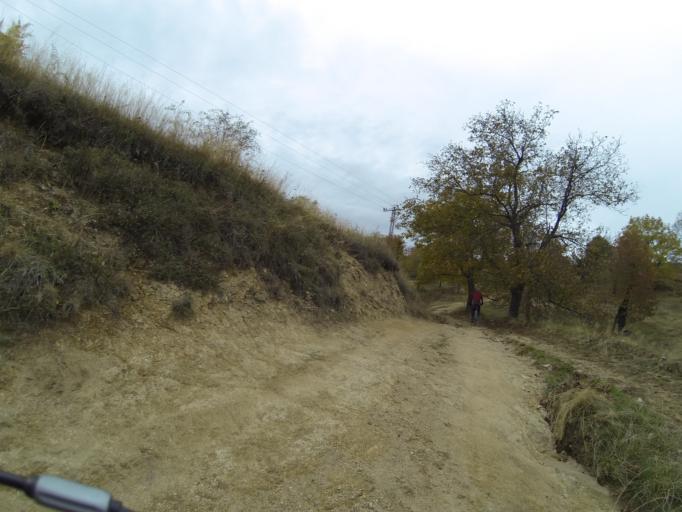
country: RO
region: Gorj
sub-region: Comuna Pades
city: Closani
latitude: 45.1117
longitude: 22.8479
